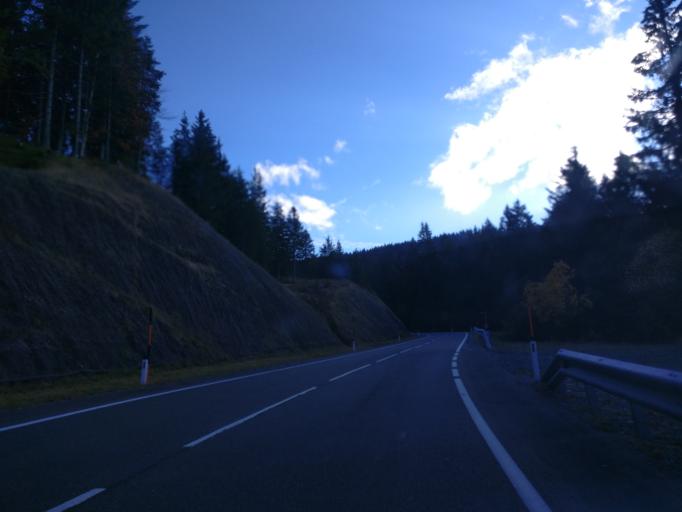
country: AT
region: Salzburg
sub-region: Politischer Bezirk Zell am See
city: Dienten am Hochkonig
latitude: 47.4027
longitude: 12.9930
